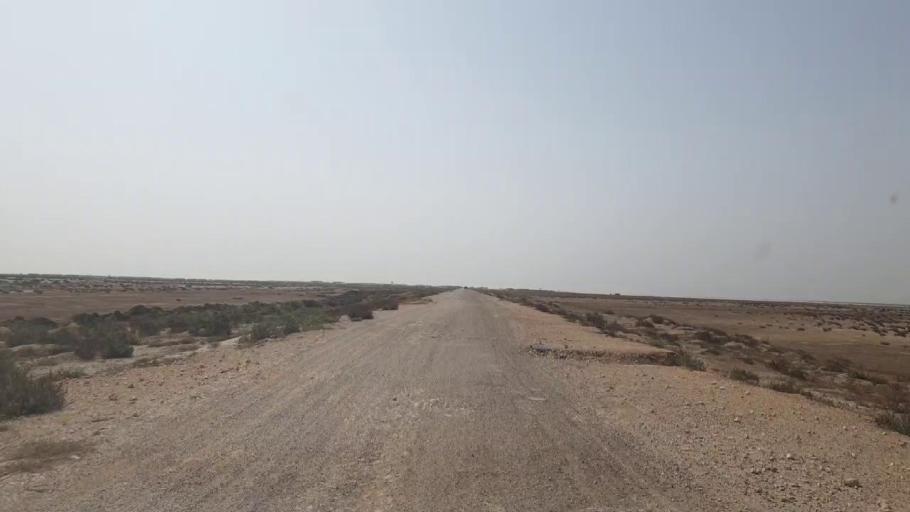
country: PK
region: Sindh
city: Jati
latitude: 24.3526
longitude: 68.5938
